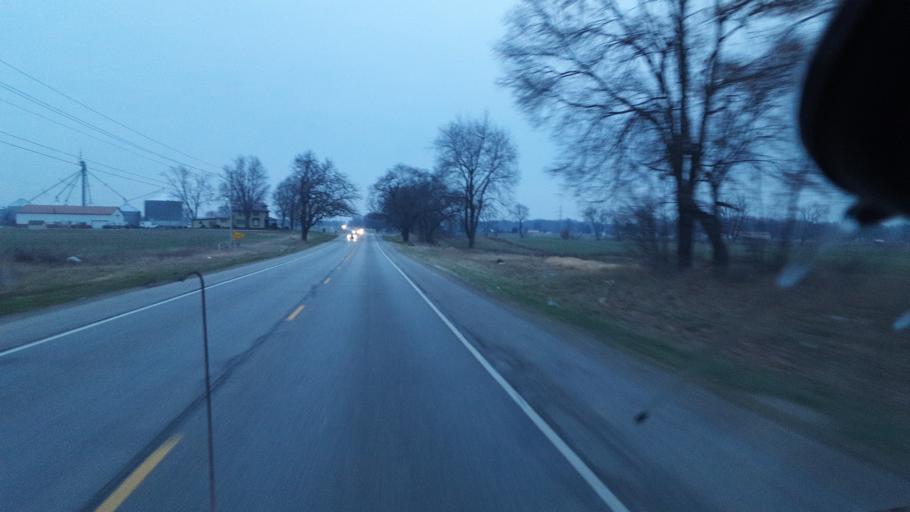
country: US
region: Indiana
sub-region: Elkhart County
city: Bristol
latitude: 41.6676
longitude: -85.7822
